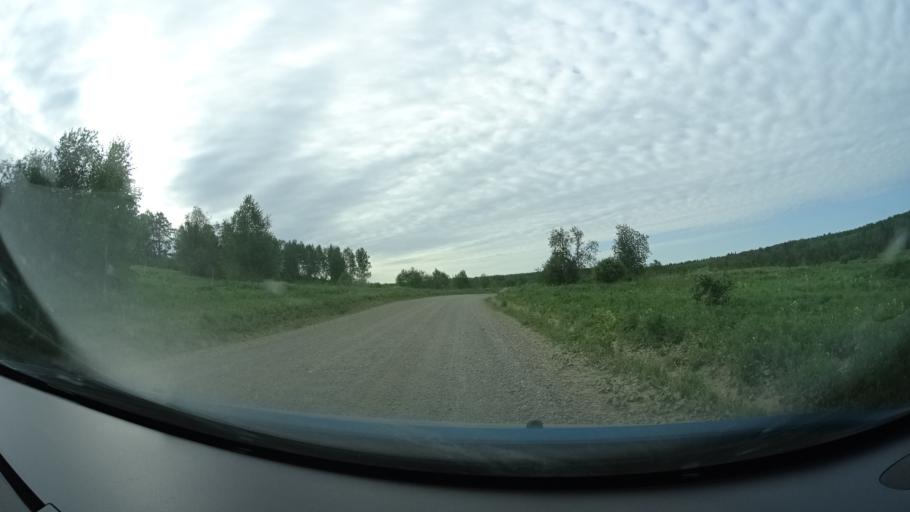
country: RU
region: Perm
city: Kuyeda
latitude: 56.6435
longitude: 55.7052
